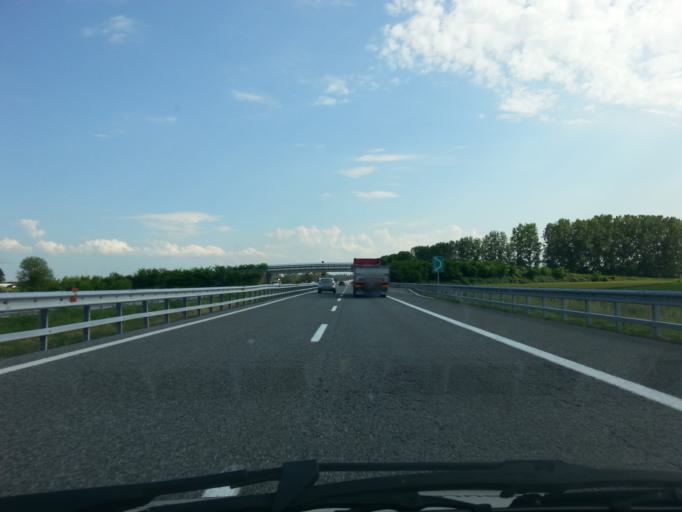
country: IT
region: Piedmont
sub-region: Provincia di Cuneo
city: Caramagna Piemonte
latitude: 44.7946
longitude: 7.7527
